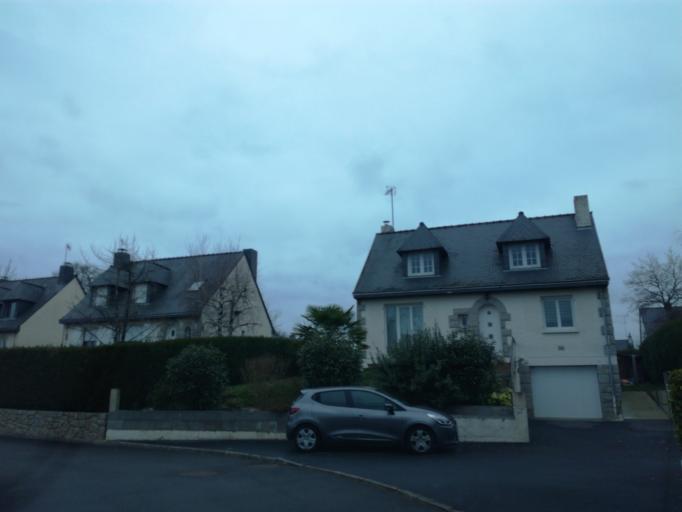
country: FR
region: Brittany
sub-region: Departement d'Ille-et-Vilaine
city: Chantepie
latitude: 48.0906
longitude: -1.6069
